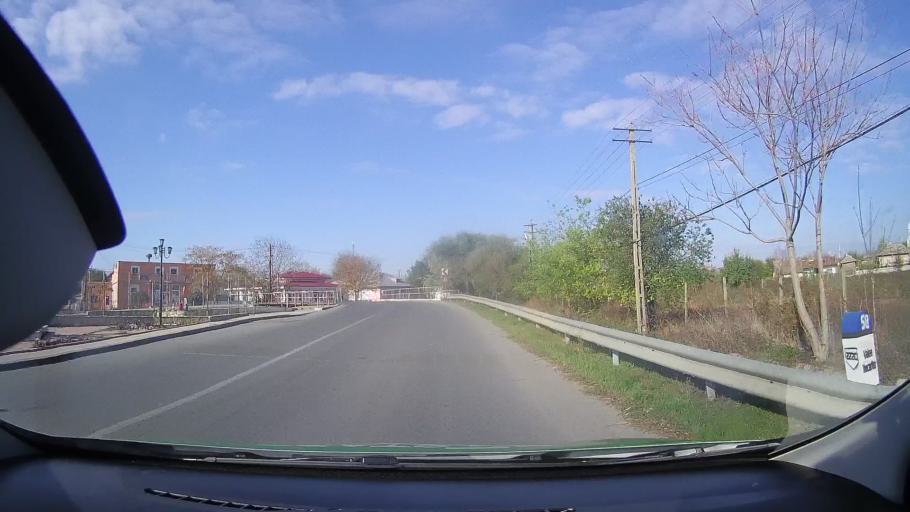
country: RO
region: Tulcea
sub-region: Comuna Valea Nucarilor
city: Valea Nucarilor
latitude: 45.0399
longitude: 28.9375
